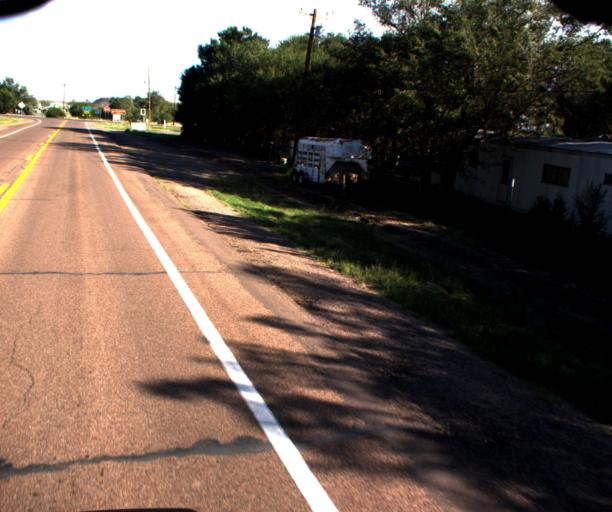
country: US
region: Arizona
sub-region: Apache County
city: Springerville
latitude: 34.1316
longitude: -109.2690
